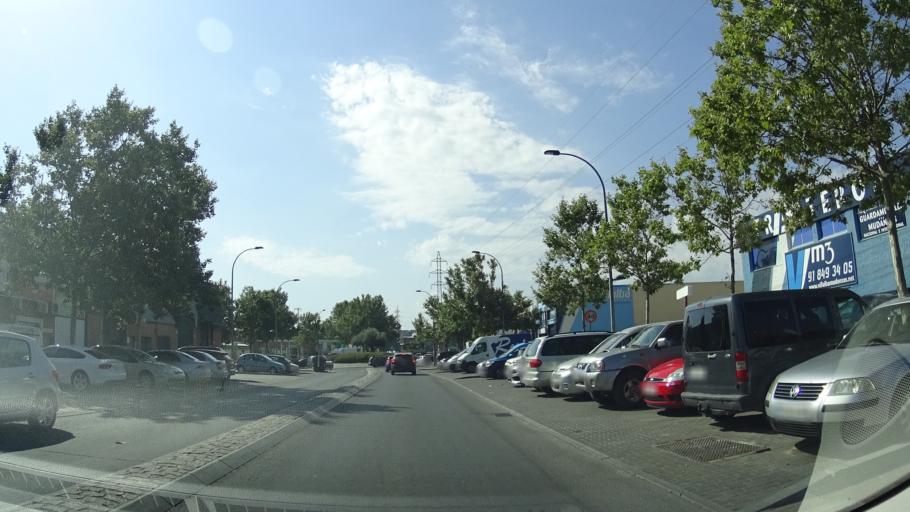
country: ES
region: Madrid
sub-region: Provincia de Madrid
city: Collado-Villalba
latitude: 40.6289
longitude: -4.0197
